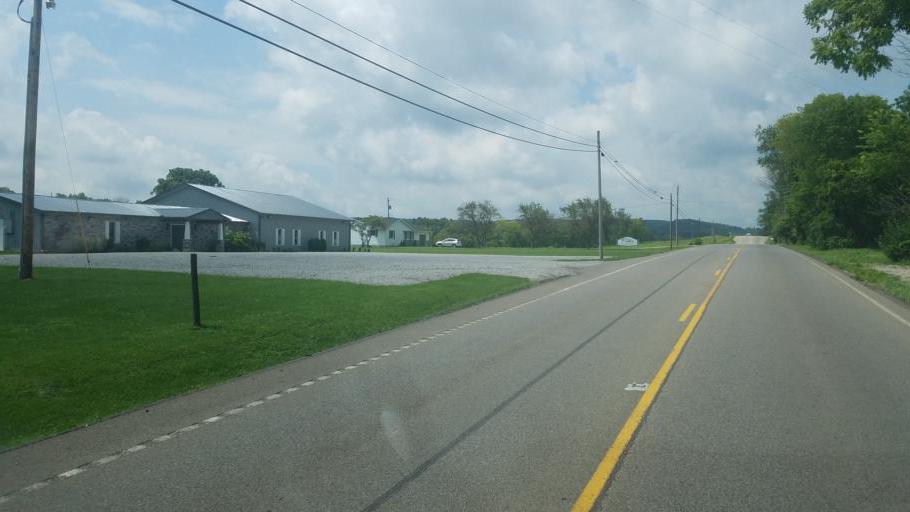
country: US
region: Ohio
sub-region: Fairfield County
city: Lancaster
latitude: 39.6924
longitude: -82.6490
